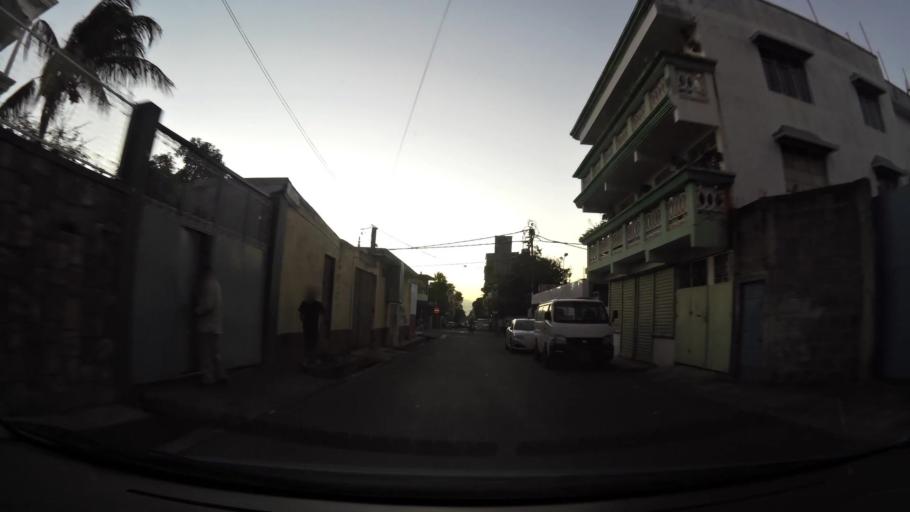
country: MU
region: Port Louis
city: Port Louis
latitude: -20.1669
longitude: 57.5168
